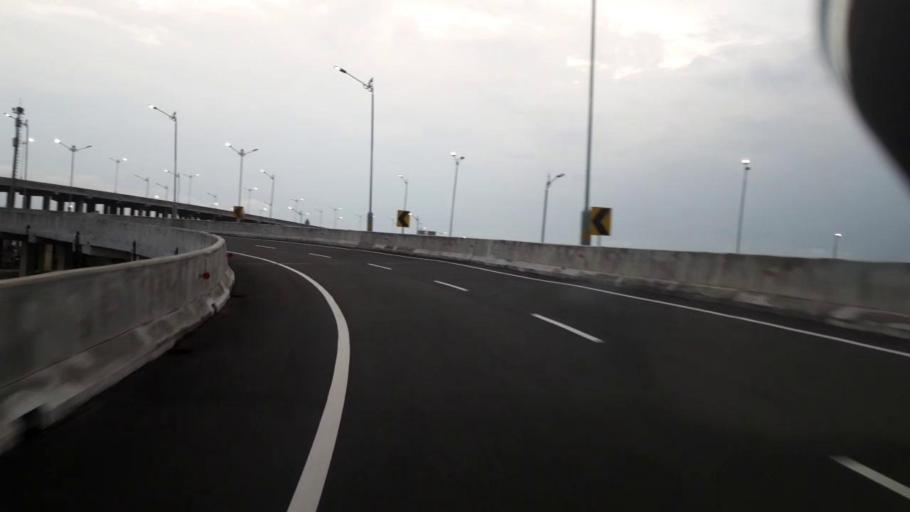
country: ID
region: Bali
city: Kelanabian
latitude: -8.7435
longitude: 115.1969
